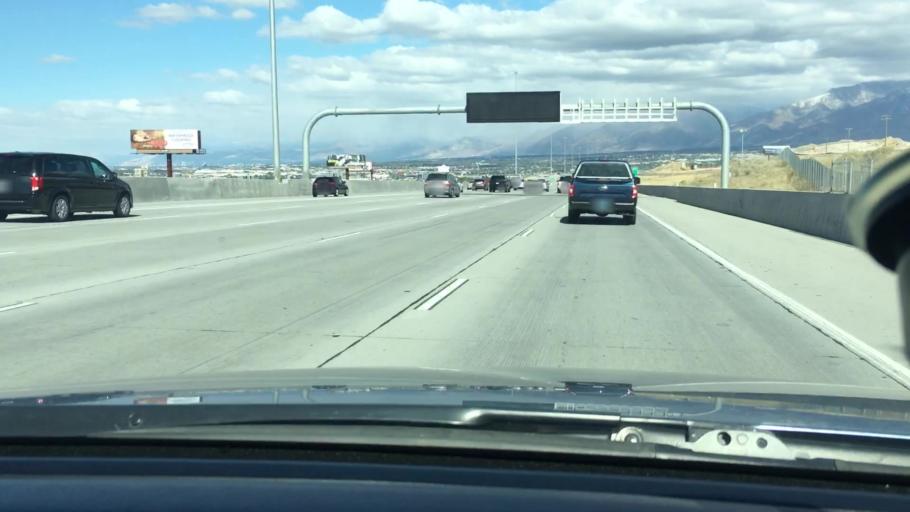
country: US
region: Utah
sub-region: Salt Lake County
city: Bluffdale
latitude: 40.4708
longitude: -111.9085
